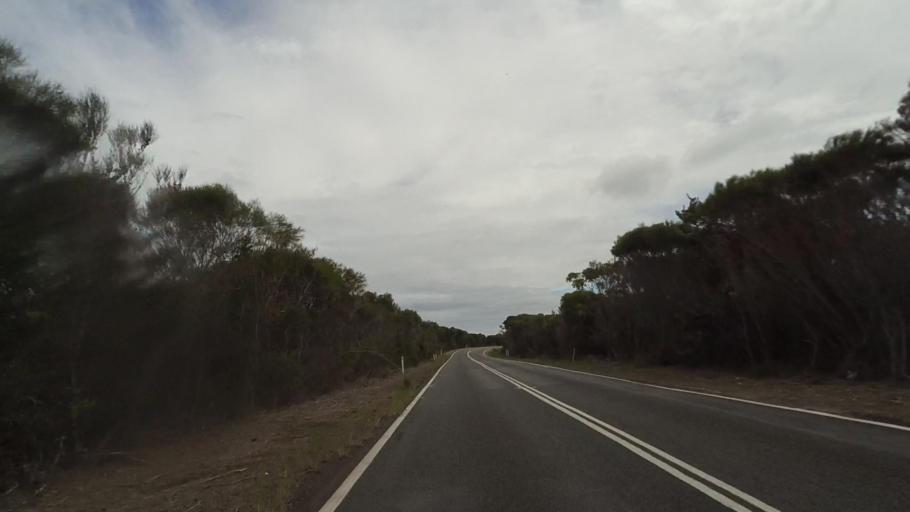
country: AU
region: New South Wales
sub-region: Sutherland Shire
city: Bundeena
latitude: -34.1006
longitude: 151.1223
